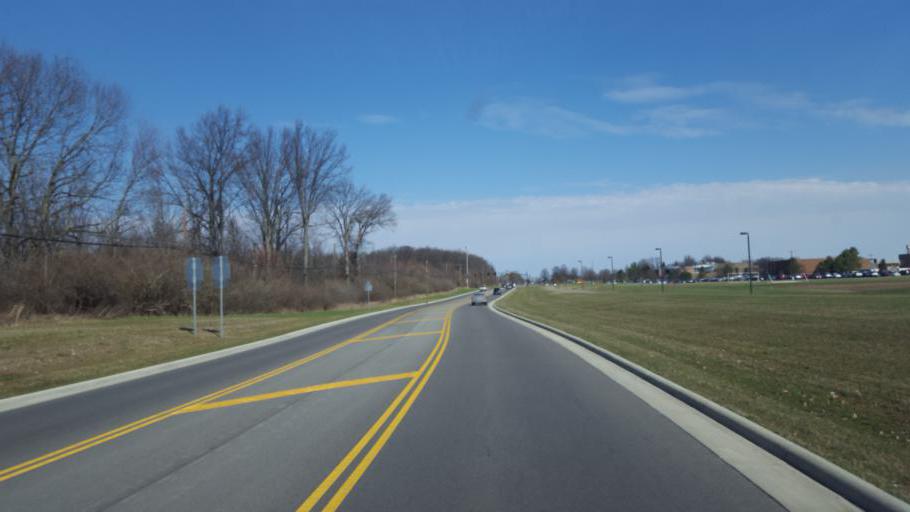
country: US
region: Ohio
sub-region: Marion County
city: Marion
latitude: 40.5739
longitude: -83.0926
